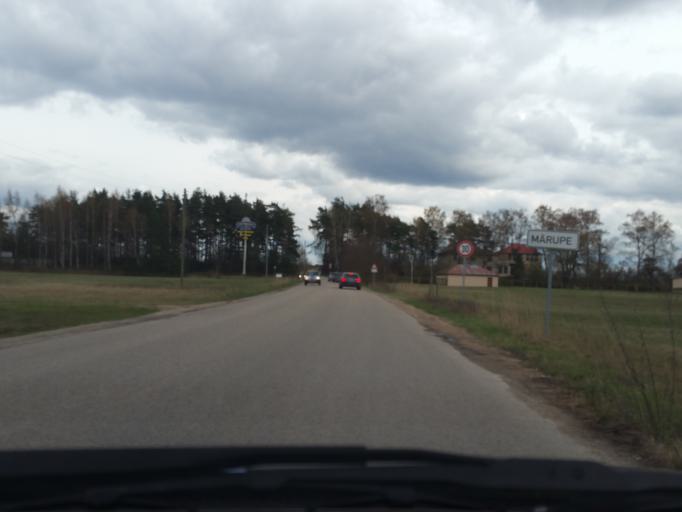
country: LV
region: Marupe
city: Marupe
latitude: 56.9224
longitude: 23.9961
